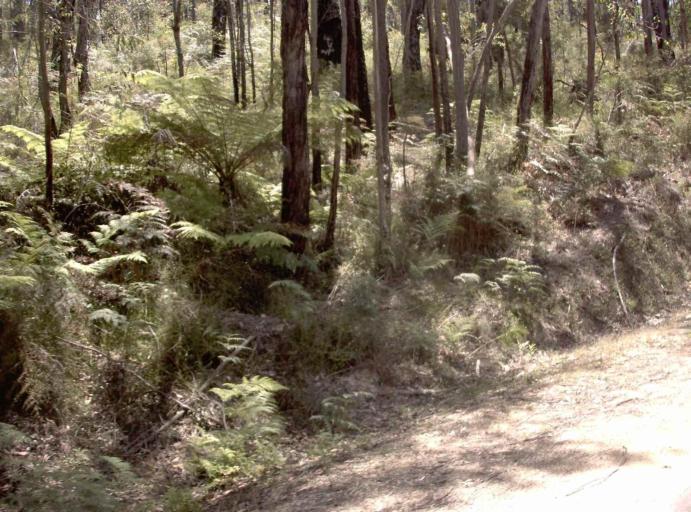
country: AU
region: New South Wales
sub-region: Bombala
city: Bombala
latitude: -37.5594
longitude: 148.9437
